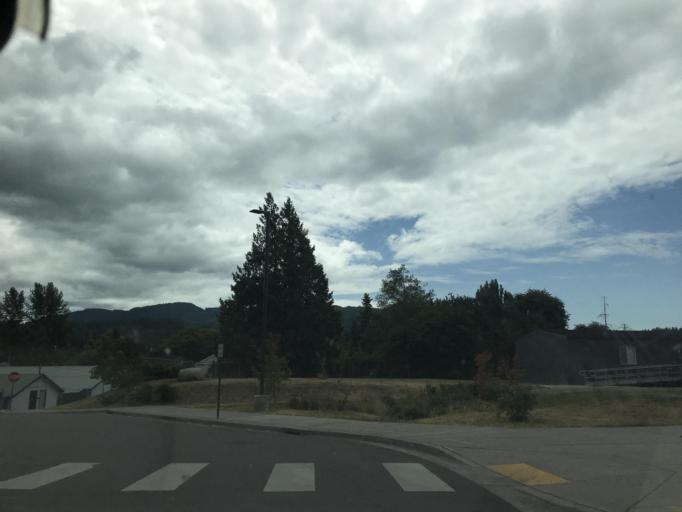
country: US
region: Washington
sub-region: Whatcom County
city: Bellingham
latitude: 48.7224
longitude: -122.4831
